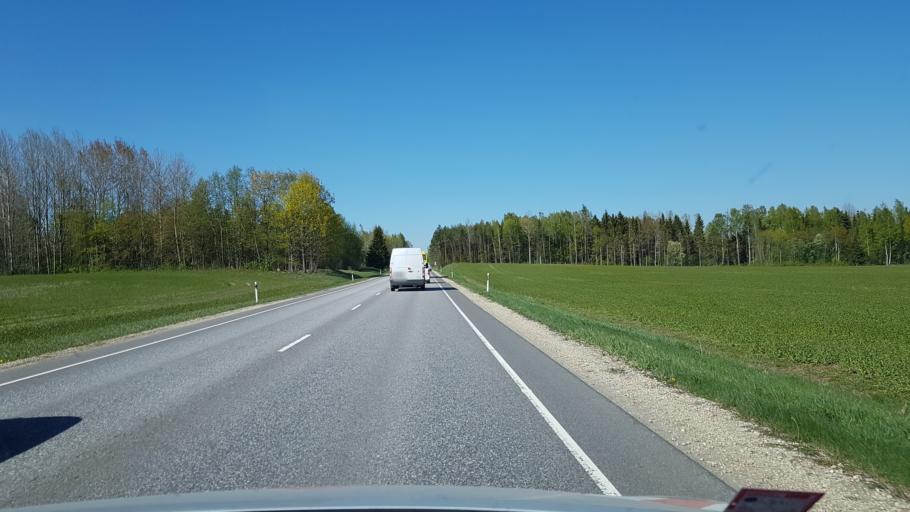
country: EE
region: Tartu
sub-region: UElenurme vald
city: Ulenurme
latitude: 58.0483
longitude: 26.7297
